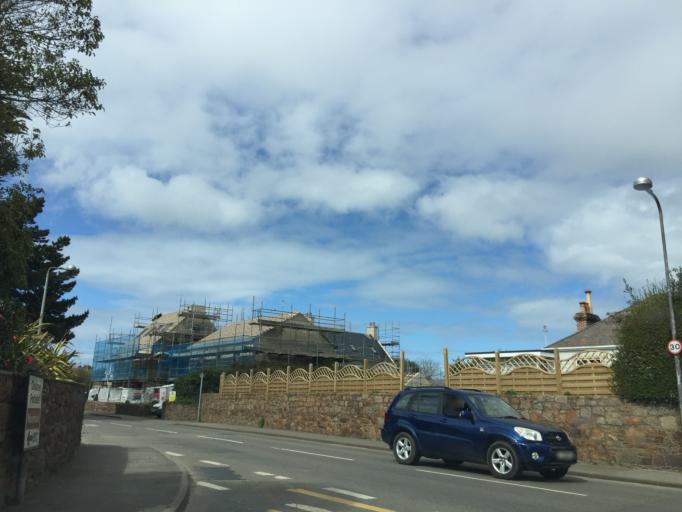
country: JE
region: St Helier
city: Saint Helier
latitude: 49.1840
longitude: -2.1799
